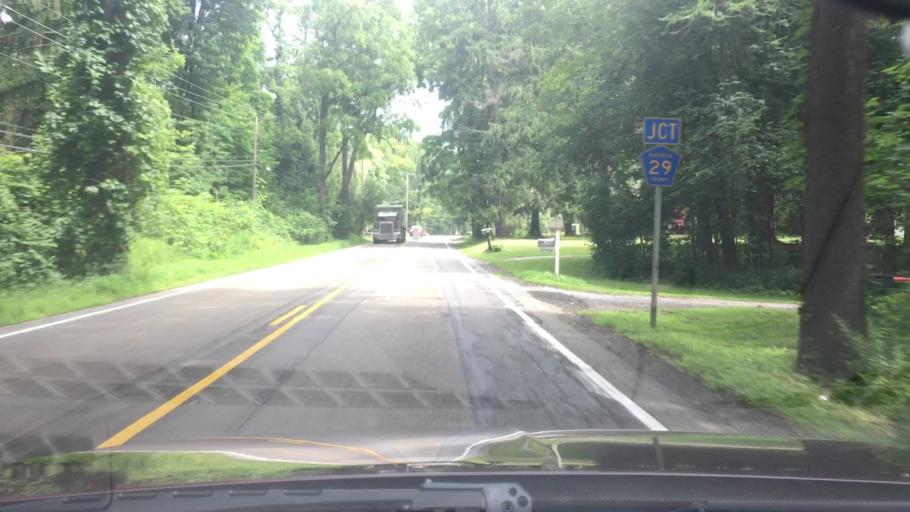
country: US
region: New York
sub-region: Dutchess County
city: Hillside Lake
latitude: 41.5610
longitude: -73.7781
